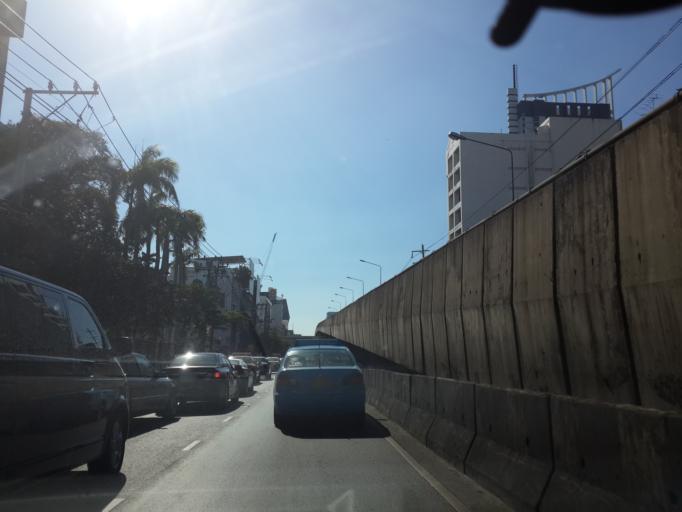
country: TH
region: Bangkok
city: Bang Kapi
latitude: 13.7615
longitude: 100.6356
